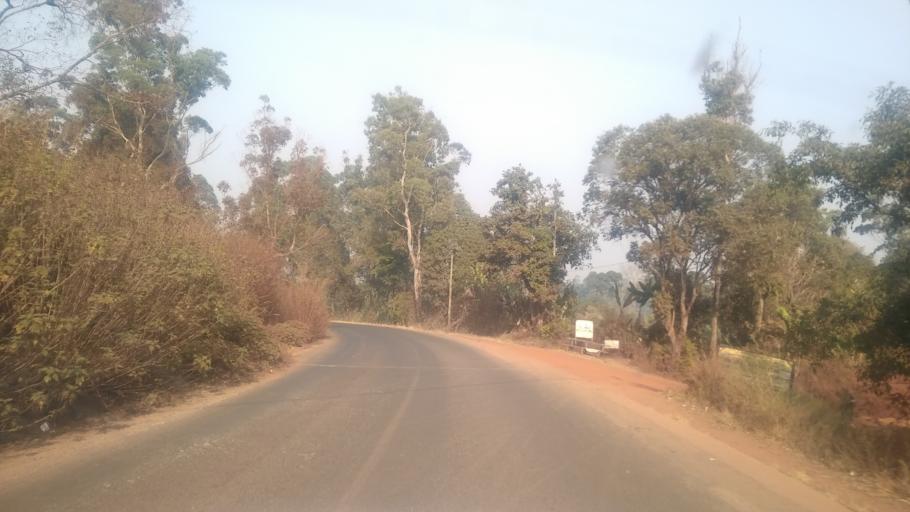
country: CM
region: West
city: Bamendjou
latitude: 5.3355
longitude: 10.3591
